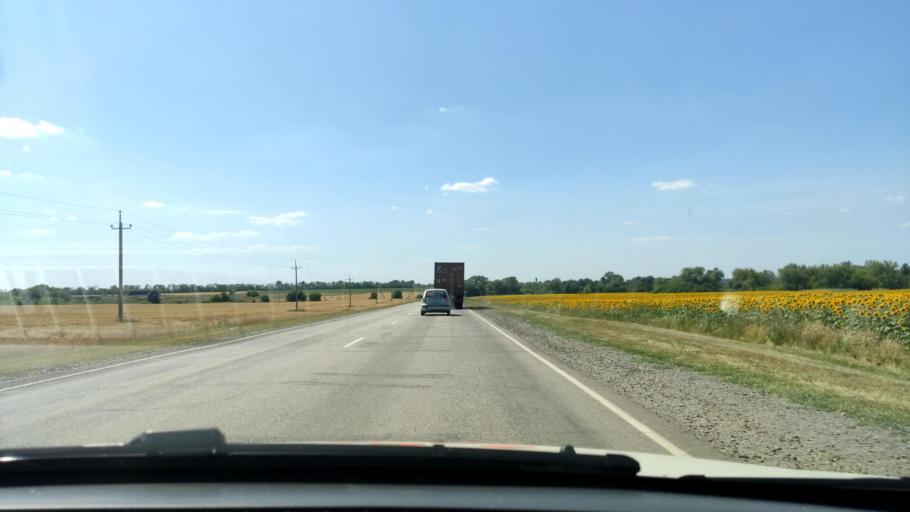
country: RU
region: Voronezj
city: Verkhnyaya Khava
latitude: 51.6781
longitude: 39.8687
